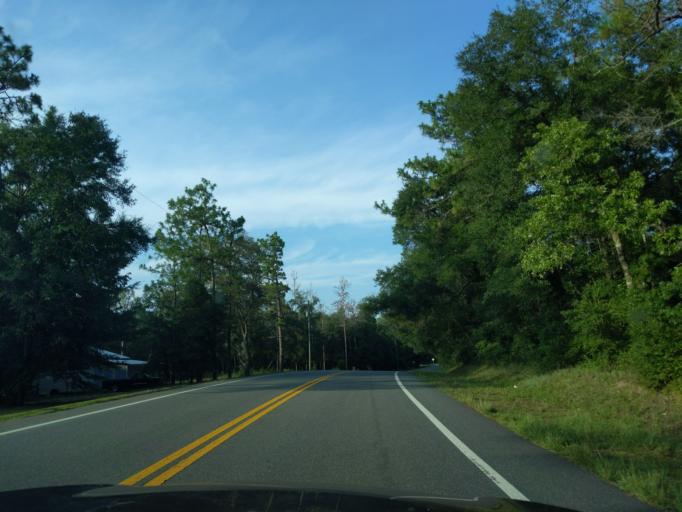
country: US
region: Florida
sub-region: Leon County
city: Tallahassee
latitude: 30.3732
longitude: -84.3607
